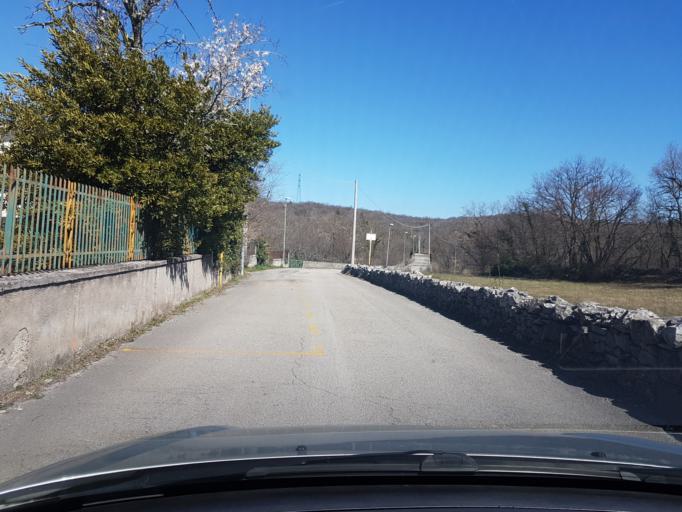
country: IT
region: Friuli Venezia Giulia
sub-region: Provincia di Trieste
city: Sistiana-Visogliano
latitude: 45.7851
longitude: 13.6434
